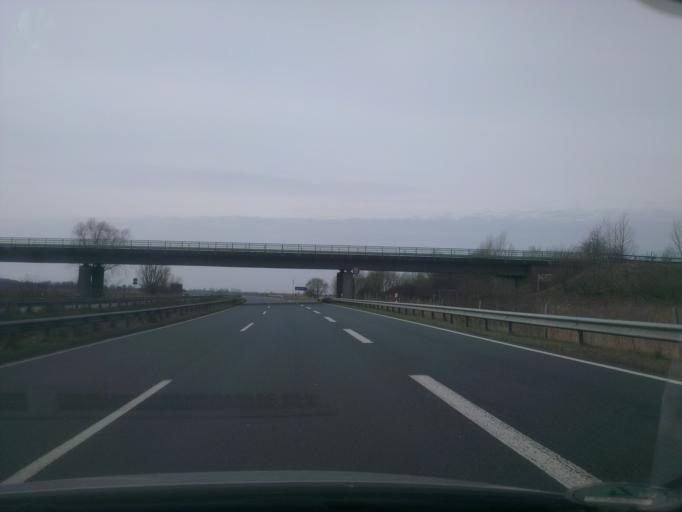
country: DE
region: Lower Saxony
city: Hinte
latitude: 53.3855
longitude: 7.1819
